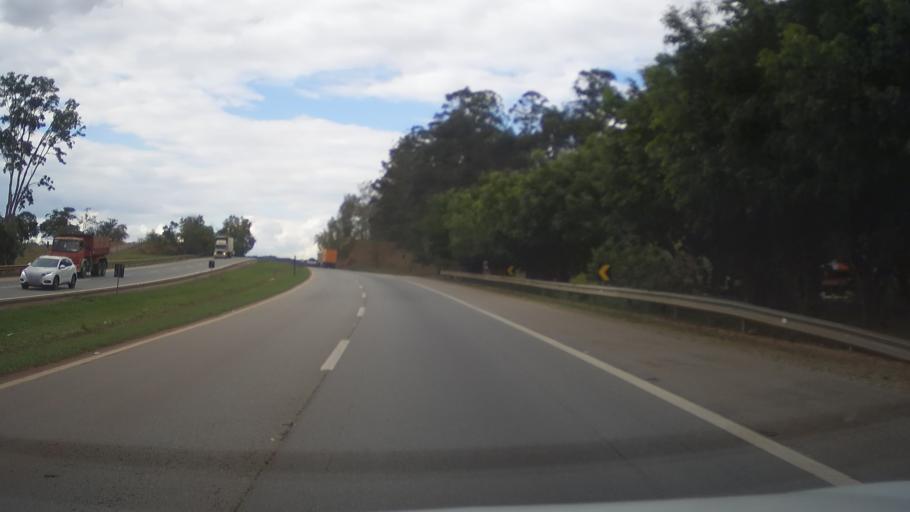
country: BR
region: Minas Gerais
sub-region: Itauna
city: Itauna
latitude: -20.2943
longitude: -44.4371
